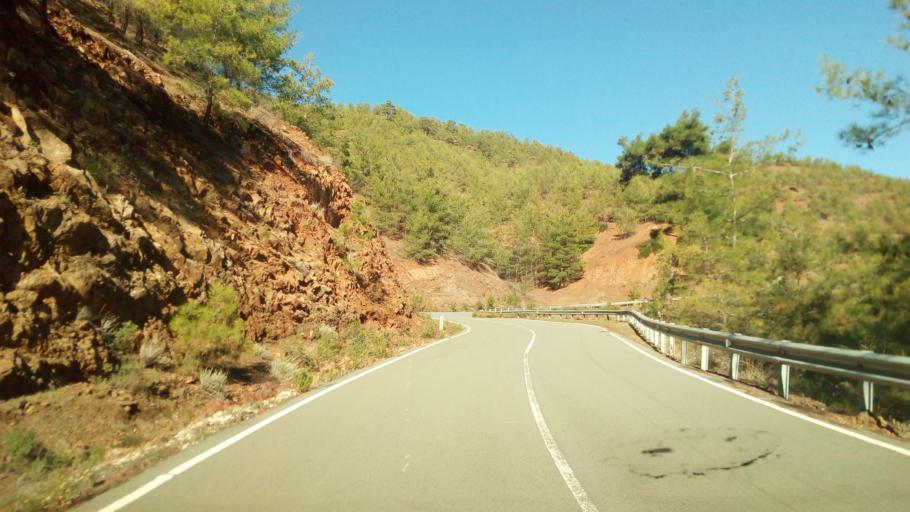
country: CY
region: Lefkosia
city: Lefka
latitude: 35.0962
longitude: 32.7577
